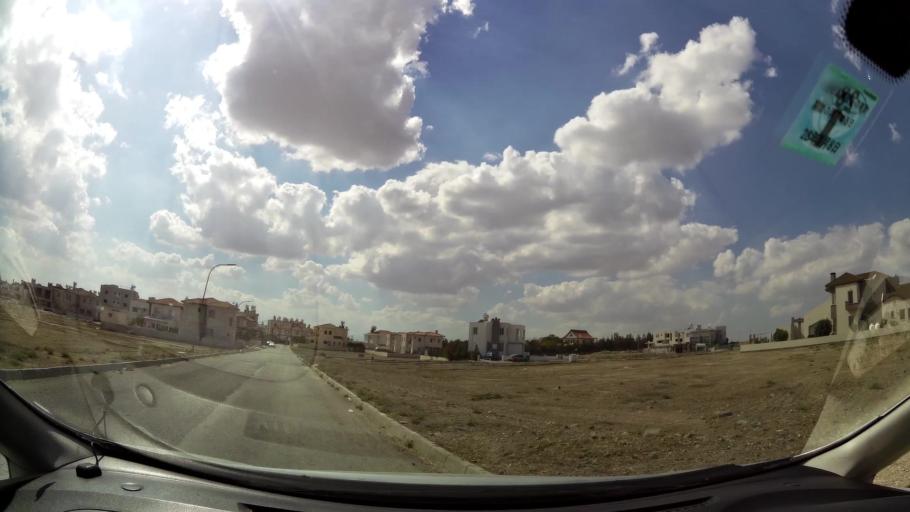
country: CY
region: Lefkosia
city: Nicosia
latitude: 35.2209
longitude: 33.2941
